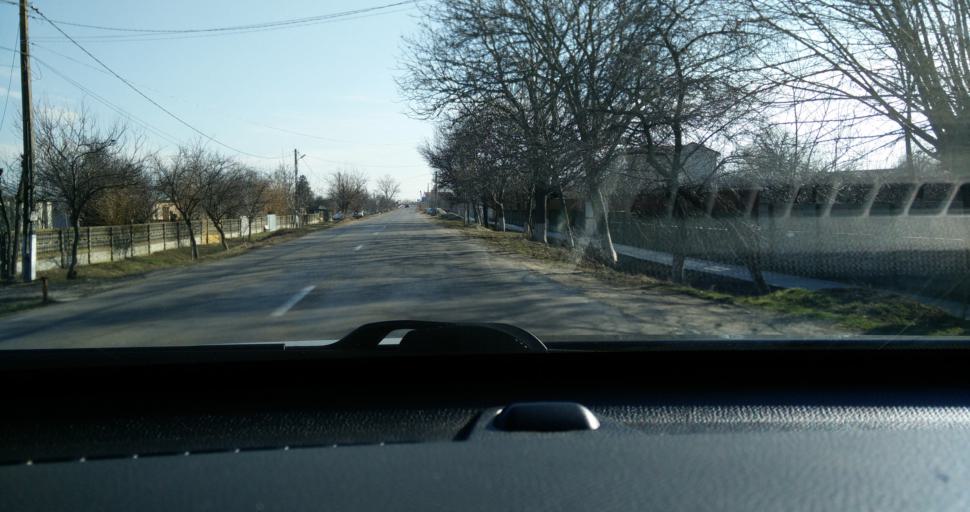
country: RO
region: Vrancea
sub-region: Comuna Maicanesti
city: Maicanesti
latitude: 45.5067
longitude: 27.4856
